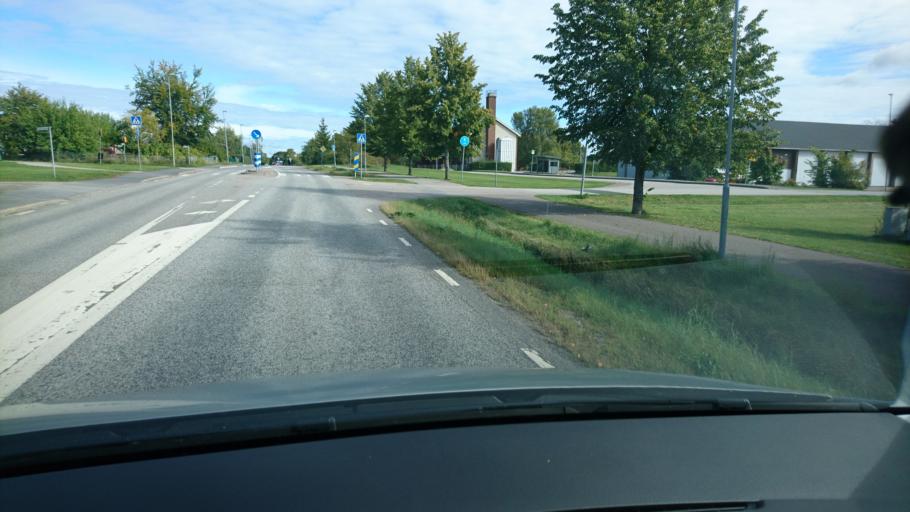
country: SE
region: Soedermanland
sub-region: Strangnas Kommun
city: Stallarholmen
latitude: 59.3555
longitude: 17.2020
